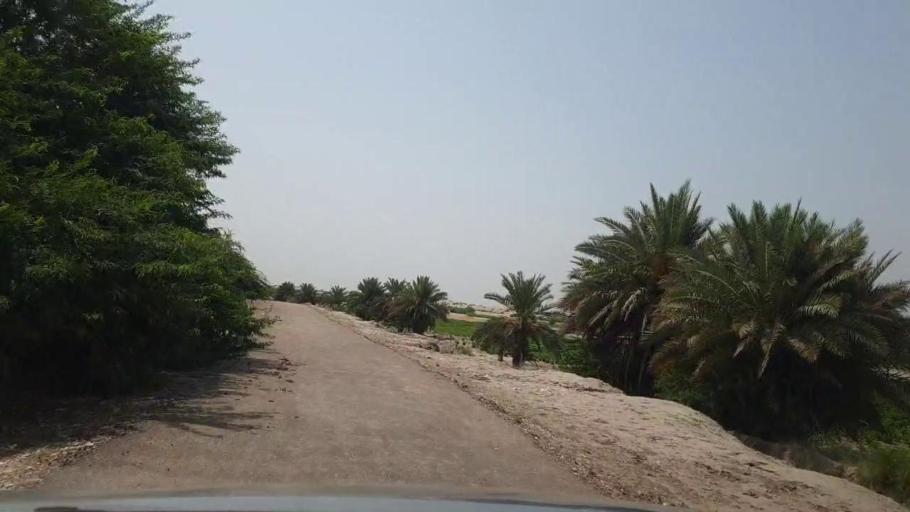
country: PK
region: Sindh
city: Pano Aqil
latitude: 27.6101
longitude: 69.1459
